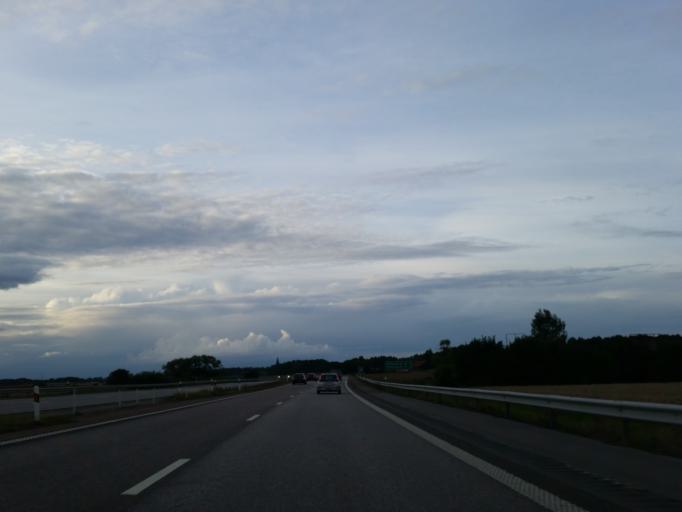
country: SE
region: Uppsala
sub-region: Uppsala Kommun
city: Saevja
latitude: 59.8132
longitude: 17.7558
